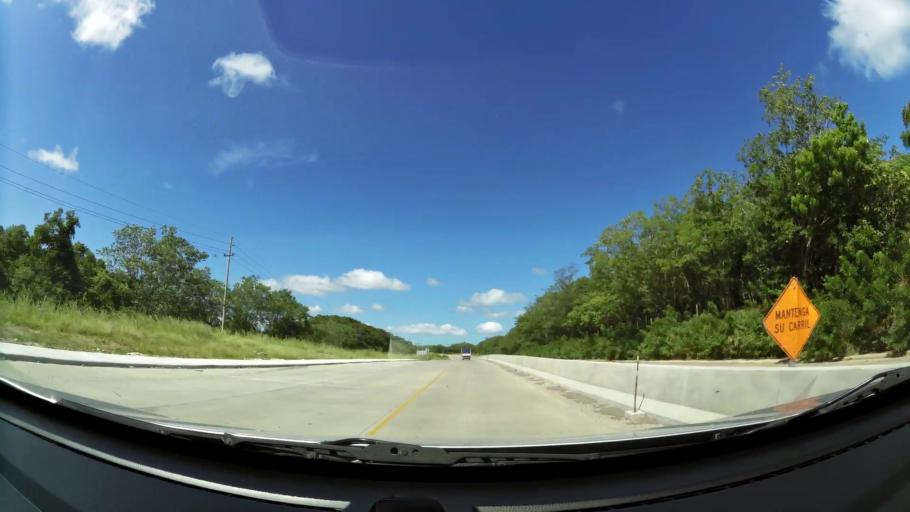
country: CR
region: Guanacaste
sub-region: Canton de Canas
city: Canas
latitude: 10.4435
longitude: -85.1117
